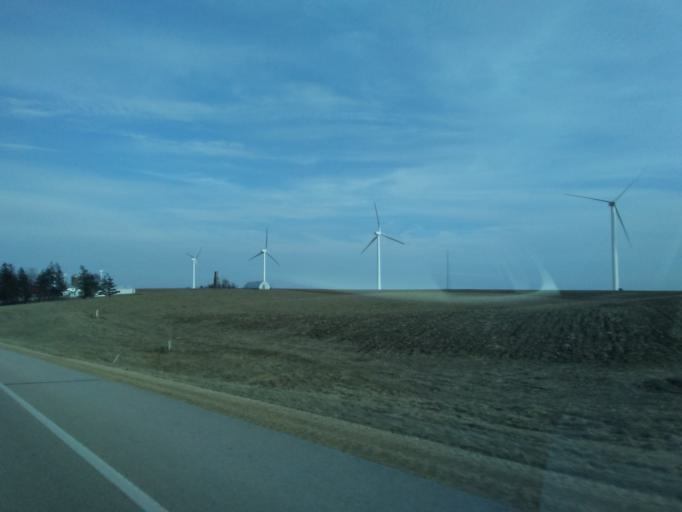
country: US
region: Wisconsin
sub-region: Grant County
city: Muscoda
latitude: 42.9662
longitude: -90.4173
